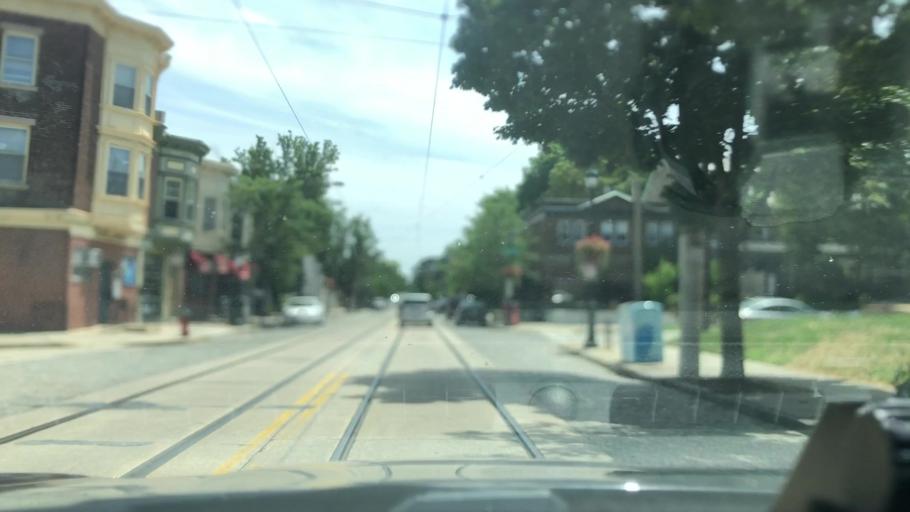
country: US
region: Pennsylvania
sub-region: Montgomery County
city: Wyndmoor
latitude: 40.0535
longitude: -75.1863
